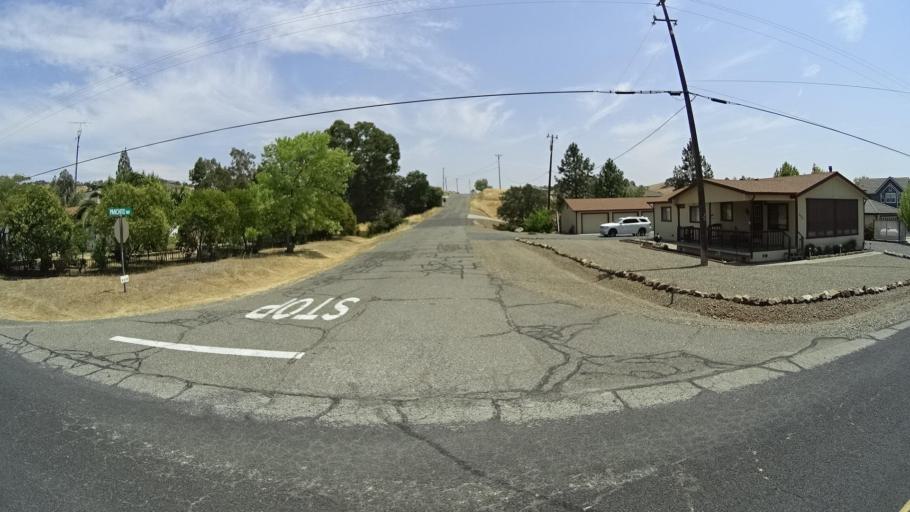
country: US
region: California
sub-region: Tuolumne County
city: Jamestown
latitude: 37.6318
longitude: -120.3525
